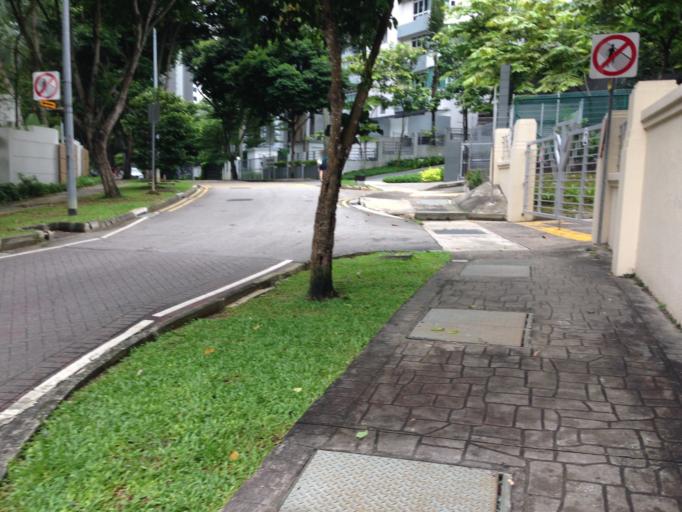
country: SG
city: Singapore
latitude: 1.3099
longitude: 103.8380
